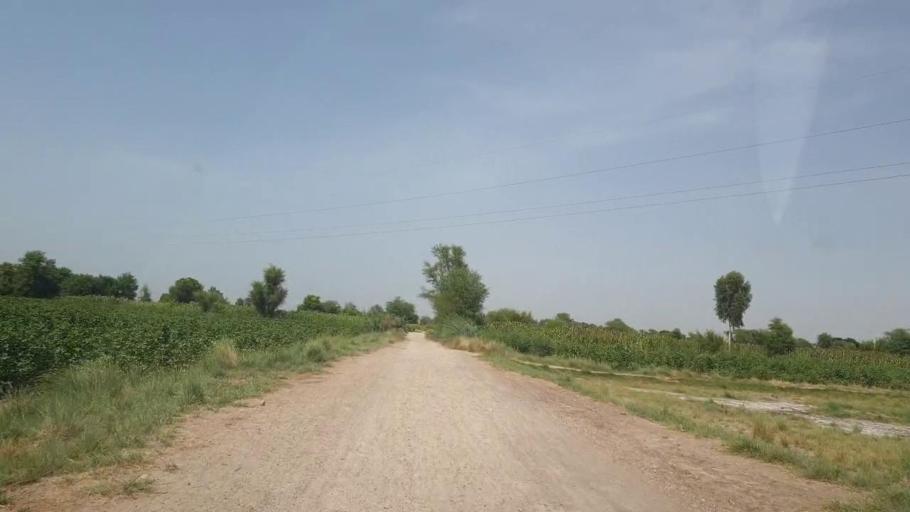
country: PK
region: Sindh
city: Bozdar
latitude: 27.0863
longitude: 68.6019
